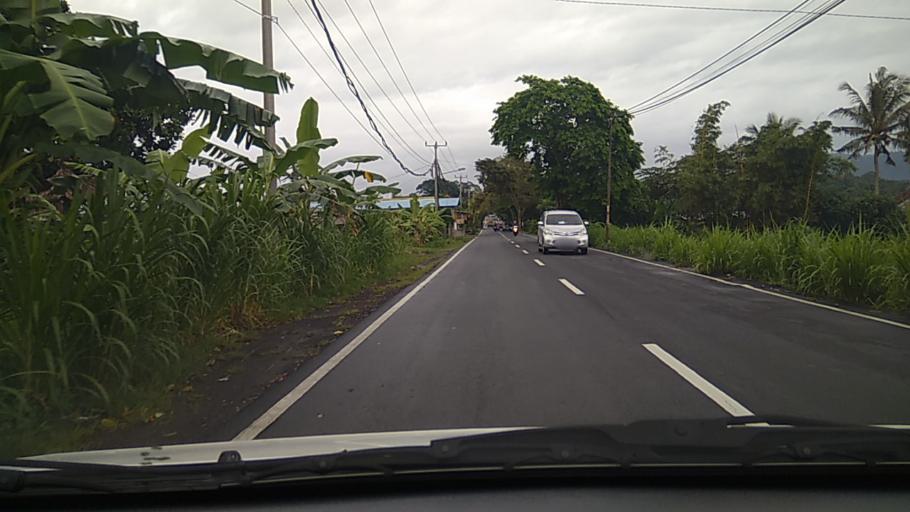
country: ID
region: Bali
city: Banjar Budakeling
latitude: -8.4311
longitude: 115.5914
